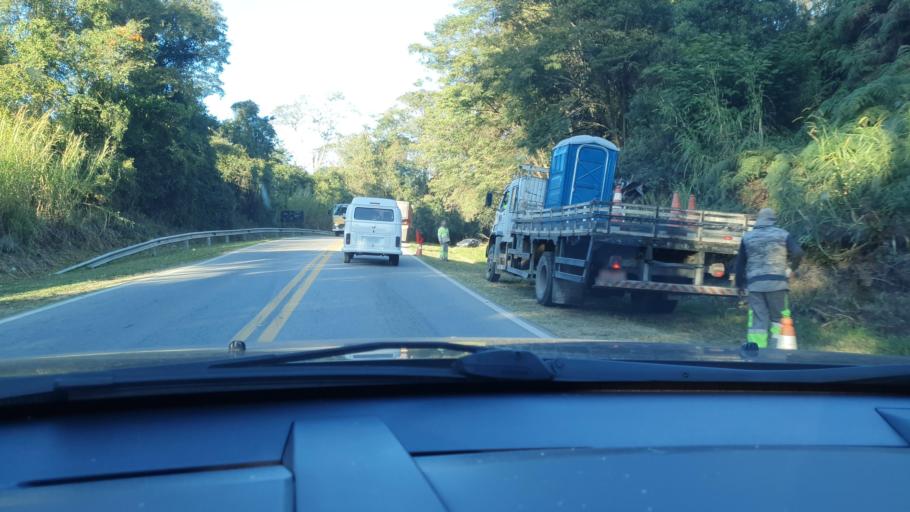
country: BR
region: Sao Paulo
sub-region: Piedade
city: Piedade
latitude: -23.7137
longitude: -47.3999
